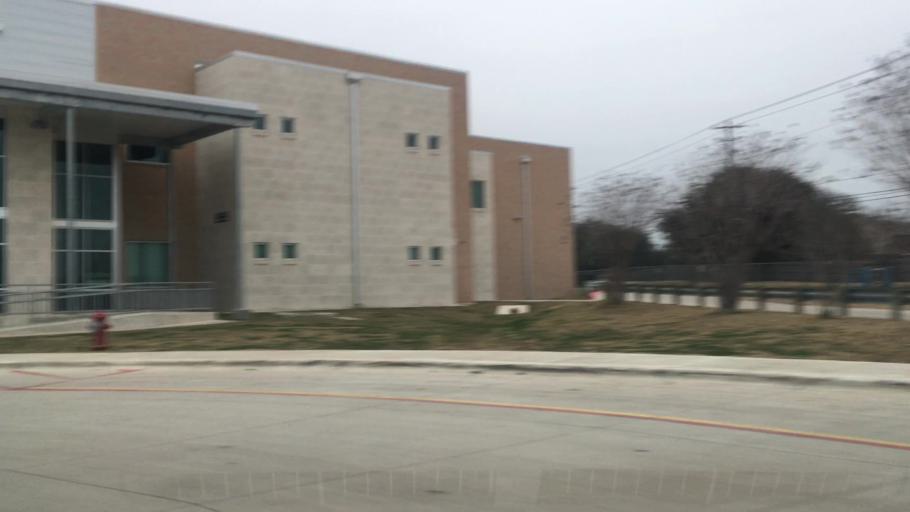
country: US
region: Texas
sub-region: Williamson County
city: Leander
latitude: 30.5390
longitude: -97.8503
